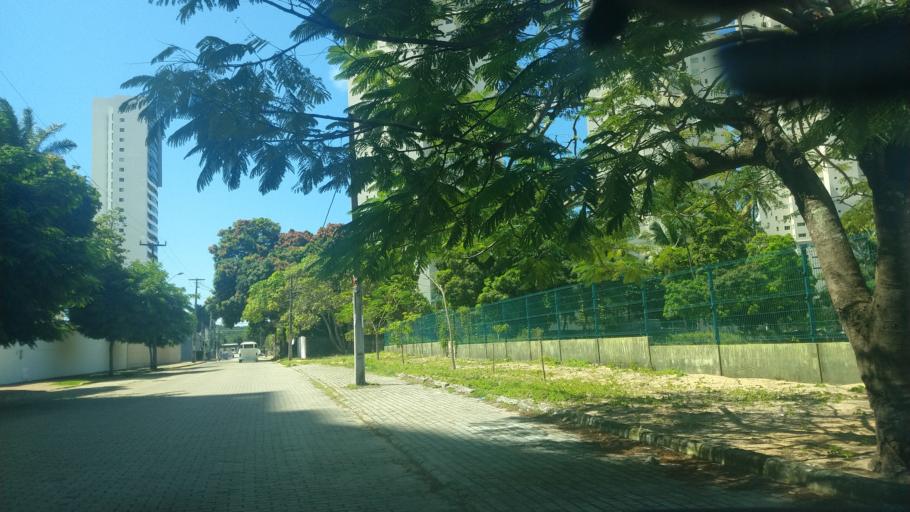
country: BR
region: Rio Grande do Norte
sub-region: Natal
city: Natal
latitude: -5.8601
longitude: -35.1983
